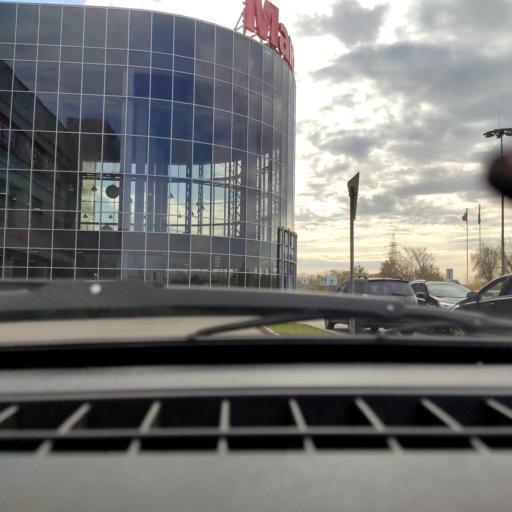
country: RU
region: Bashkortostan
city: Ufa
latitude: 54.7900
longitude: 56.0804
